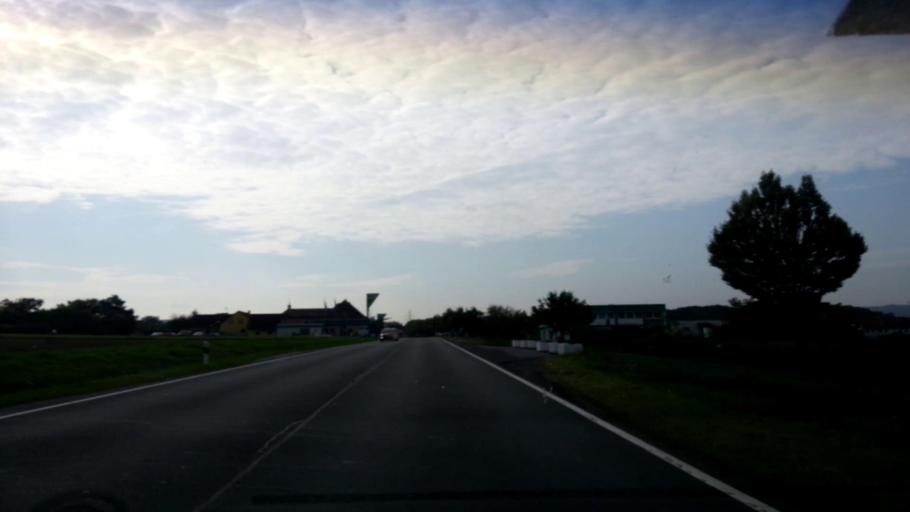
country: DE
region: Bavaria
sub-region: Regierungsbezirk Unterfranken
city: Castell
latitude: 49.7699
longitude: 10.3413
